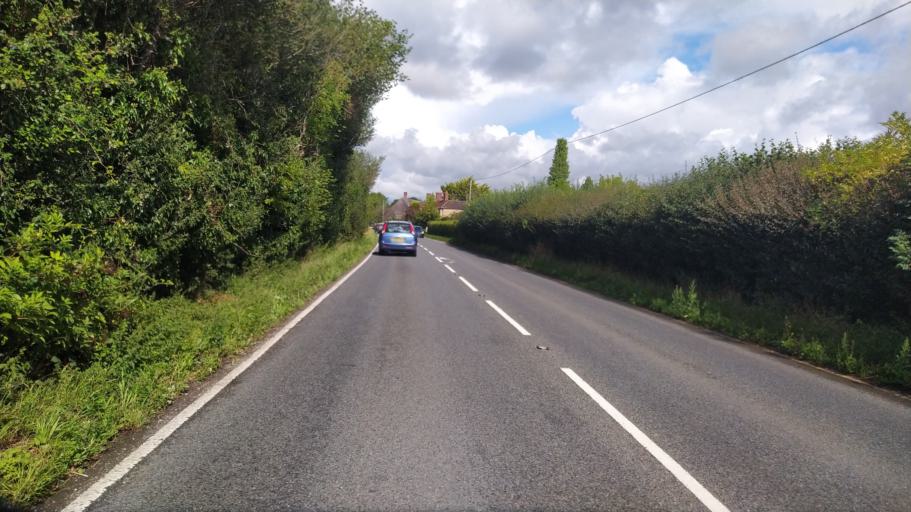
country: GB
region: England
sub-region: Dorset
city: Sturminster Newton
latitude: 50.9155
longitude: -2.2777
